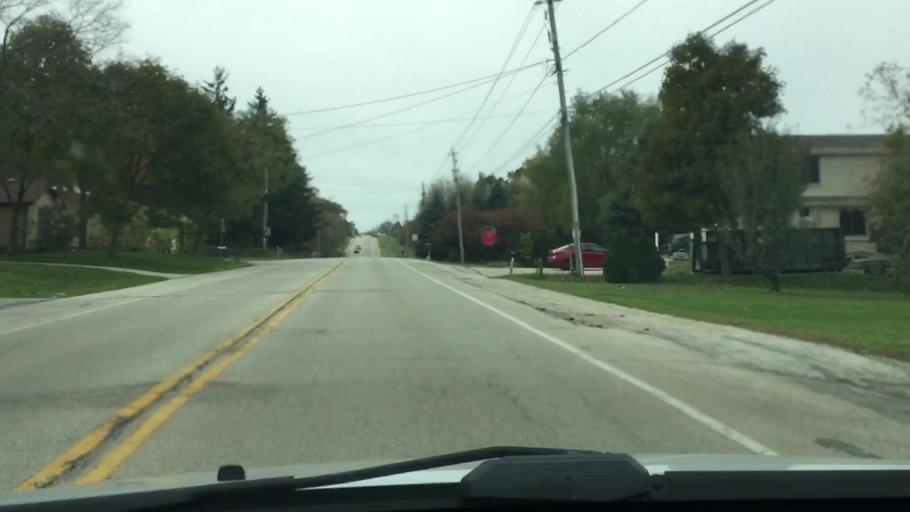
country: US
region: Wisconsin
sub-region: Waukesha County
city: Muskego
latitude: 42.9499
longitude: -88.1494
